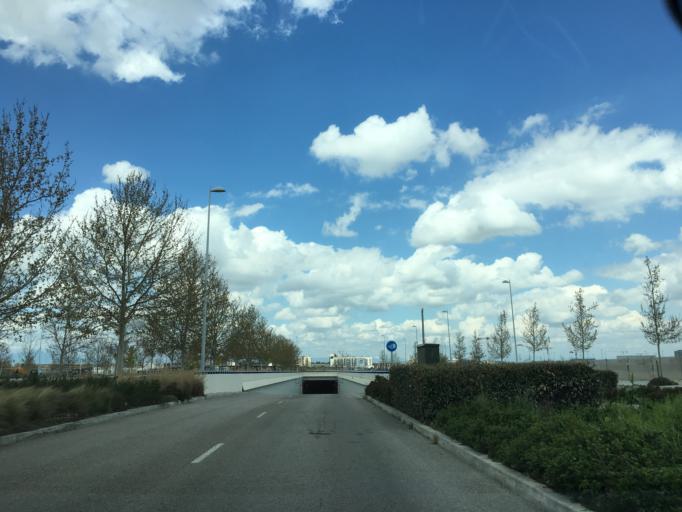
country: ES
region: Madrid
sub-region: Provincia de Madrid
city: Hortaleza
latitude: 40.4798
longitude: -3.6179
